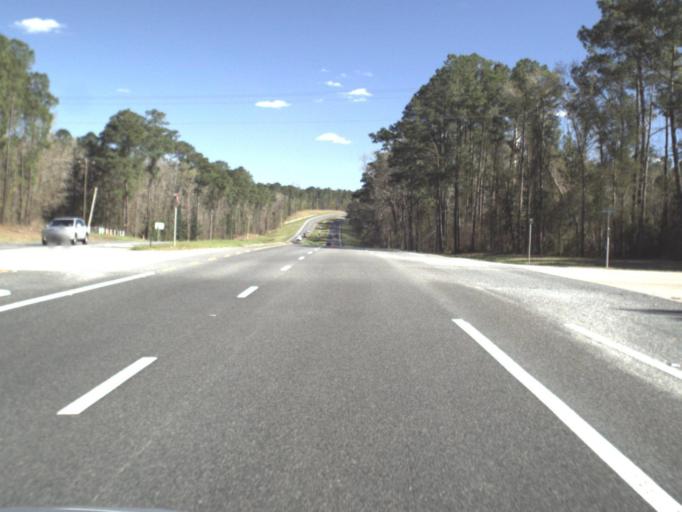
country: US
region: Florida
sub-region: Gadsden County
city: Midway
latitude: 30.5174
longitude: -84.4652
